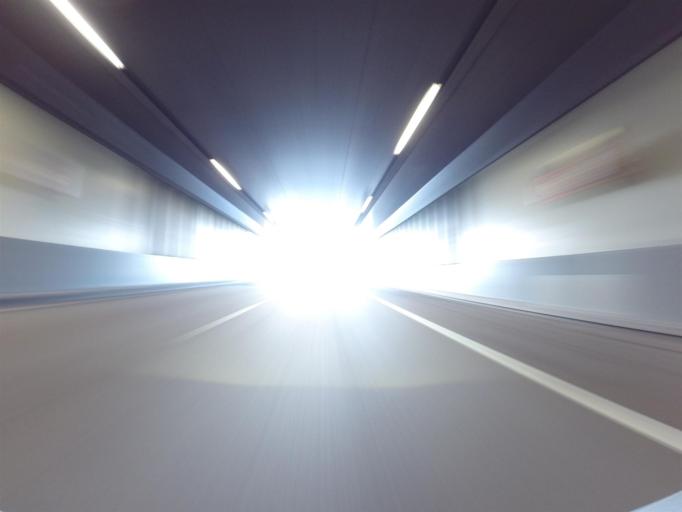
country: LU
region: Grevenmacher
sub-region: Canton de Remich
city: Mondorf-les-Bains
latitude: 49.5157
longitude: 6.2849
